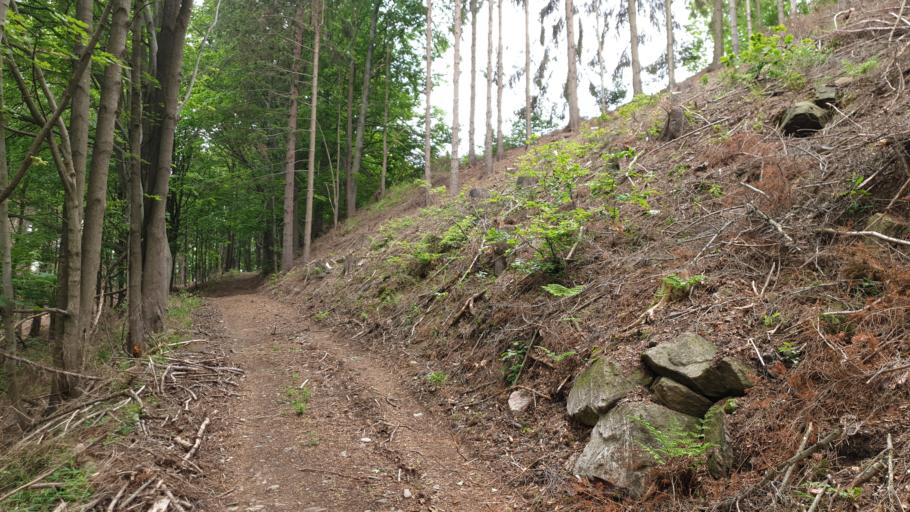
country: DE
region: Saxony
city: Barenstein
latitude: 50.8005
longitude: 13.7797
